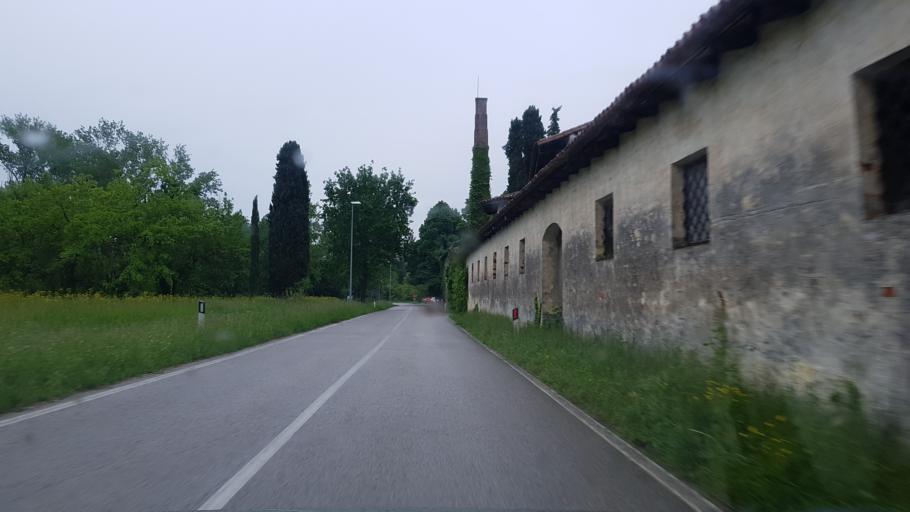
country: IT
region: Friuli Venezia Giulia
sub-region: Provincia di Udine
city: Corno di Rosazzo
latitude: 45.9863
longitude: 13.4212
